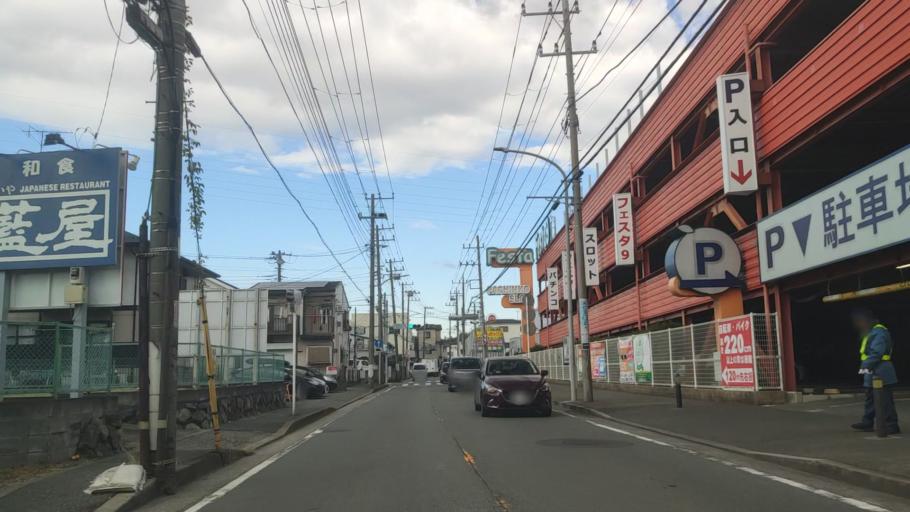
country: JP
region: Kanagawa
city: Minami-rinkan
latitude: 35.4239
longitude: 139.5309
